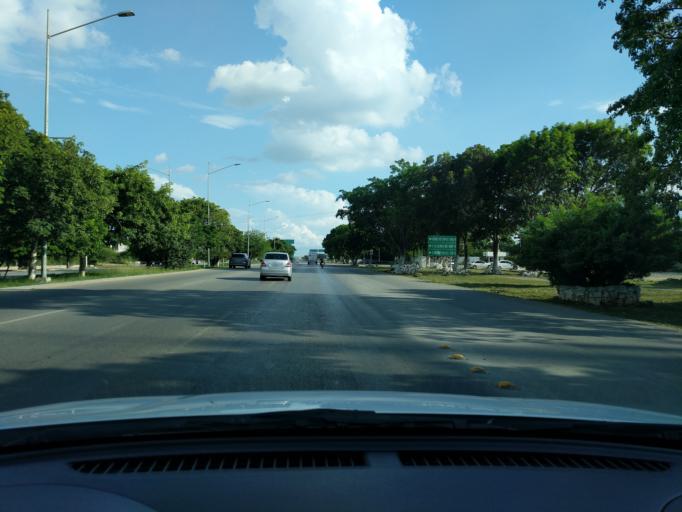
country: MX
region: Yucatan
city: Itzincab Palomeque
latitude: 20.9242
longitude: -89.6882
